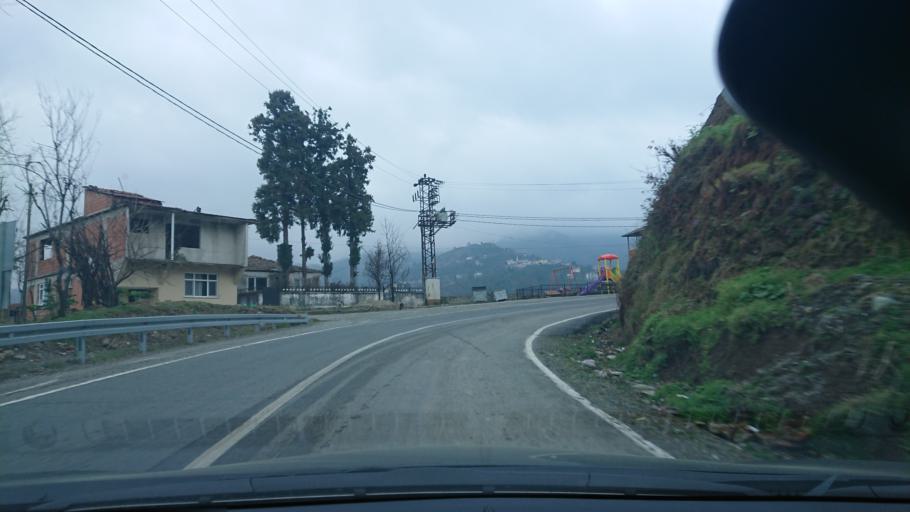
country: TR
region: Rize
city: Rize
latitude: 41.0066
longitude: 40.4883
